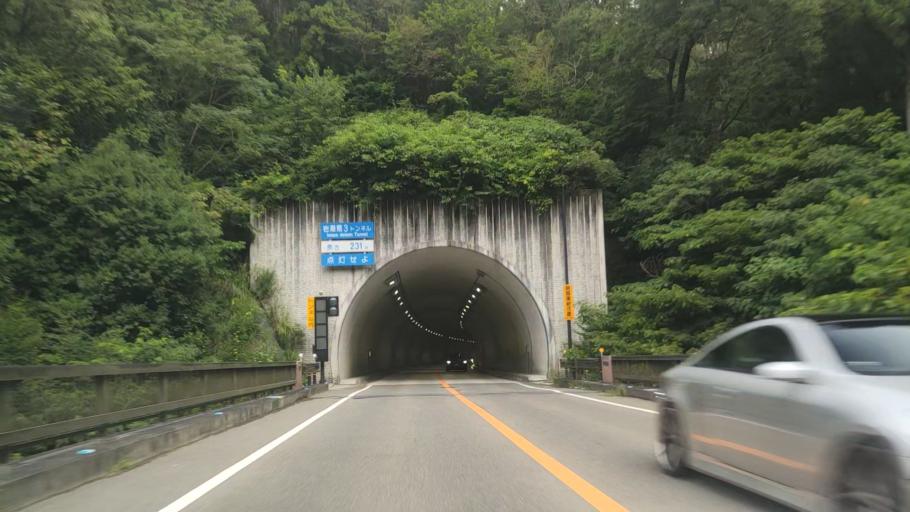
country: JP
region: Wakayama
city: Hashimoto
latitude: 34.4063
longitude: 135.5932
